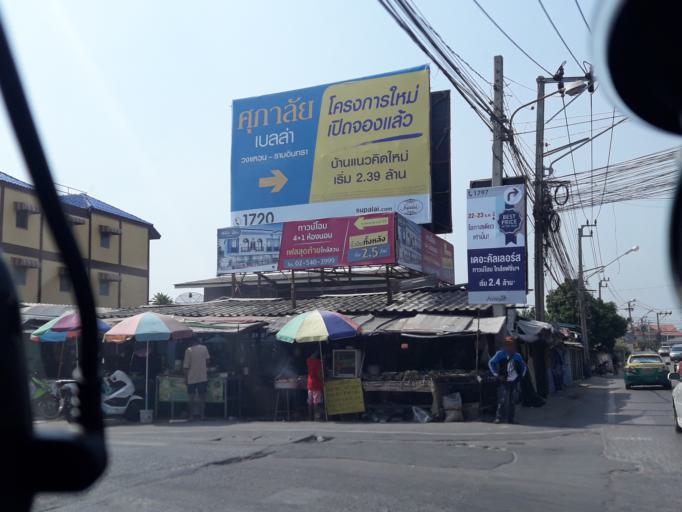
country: TH
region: Bangkok
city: Khlong Sam Wa
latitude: 13.8419
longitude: 100.7132
